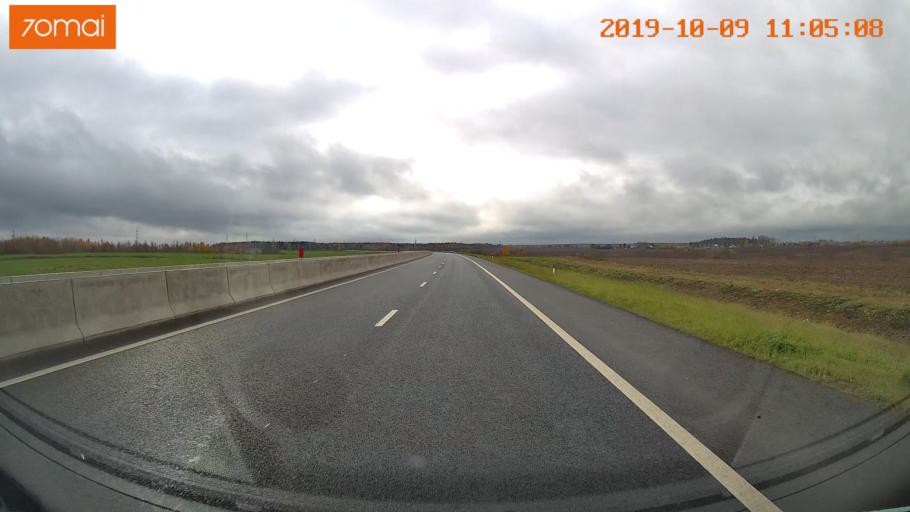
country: RU
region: Vologda
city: Molochnoye
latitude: 59.2039
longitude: 39.7595
